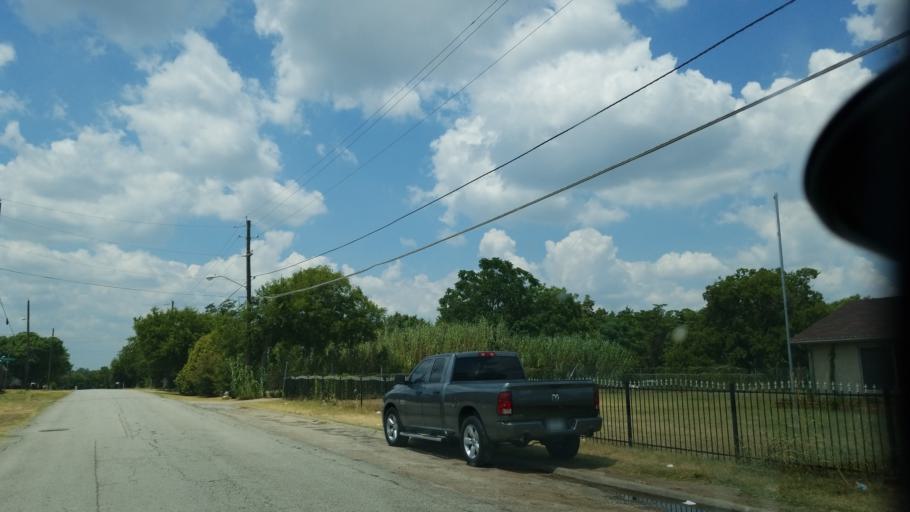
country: US
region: Texas
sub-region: Dallas County
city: Duncanville
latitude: 32.6814
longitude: -96.8993
